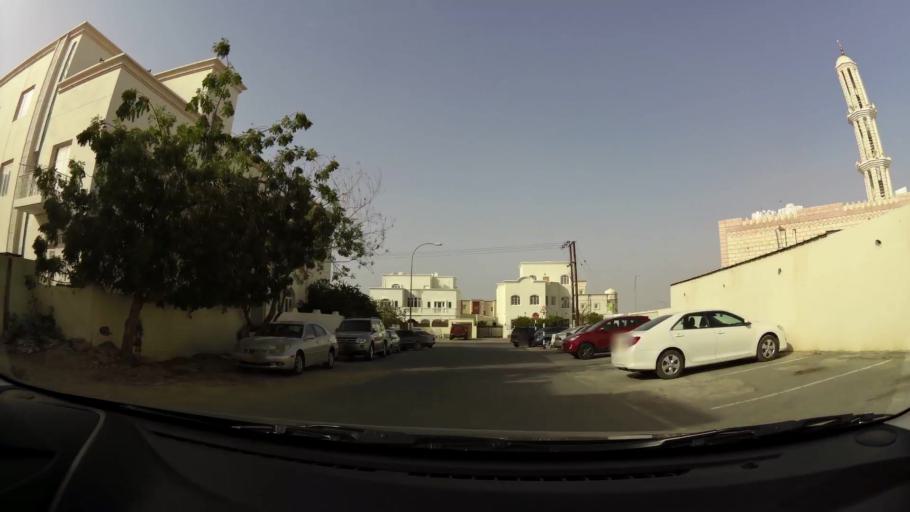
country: OM
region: Muhafazat Masqat
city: Bawshar
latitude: 23.5496
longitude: 58.3617
